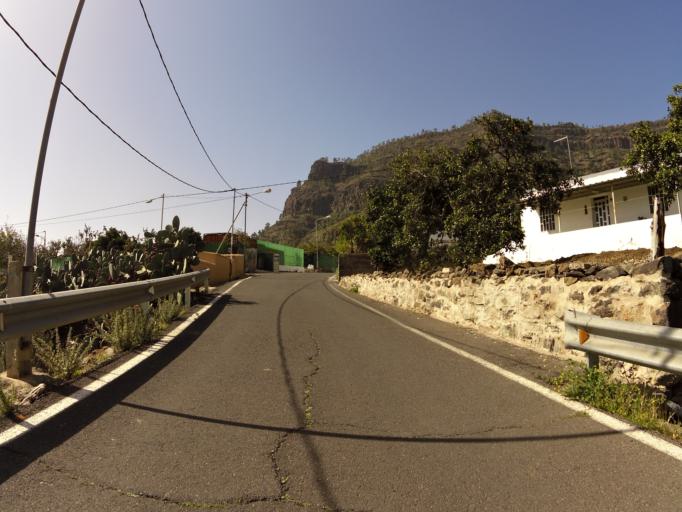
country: ES
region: Canary Islands
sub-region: Provincia de Las Palmas
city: Mogan
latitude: 27.8970
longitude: -15.6752
